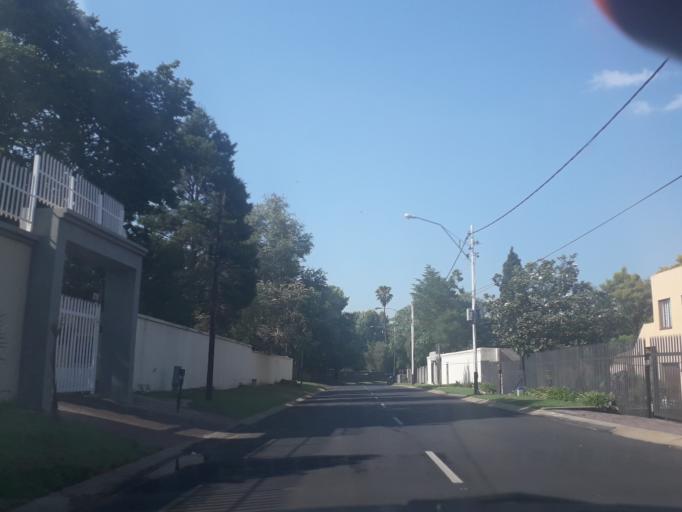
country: ZA
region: Gauteng
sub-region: City of Johannesburg Metropolitan Municipality
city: Modderfontein
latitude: -26.1113
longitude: 28.0742
